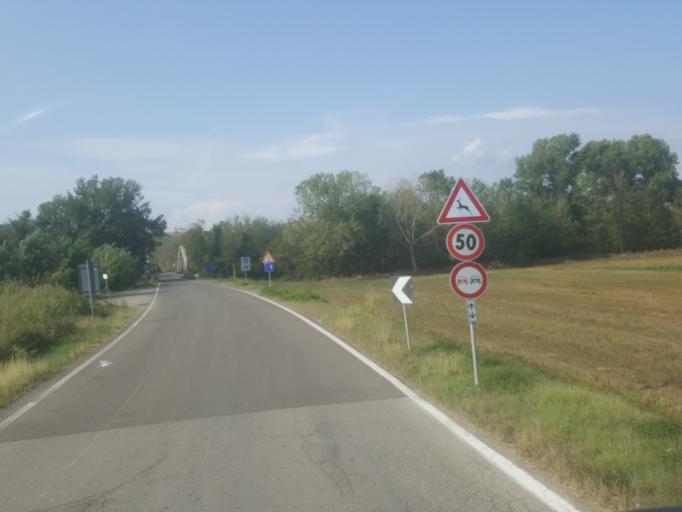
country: IT
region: Tuscany
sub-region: Province of Pisa
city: Volterra
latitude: 43.4543
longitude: 10.8305
